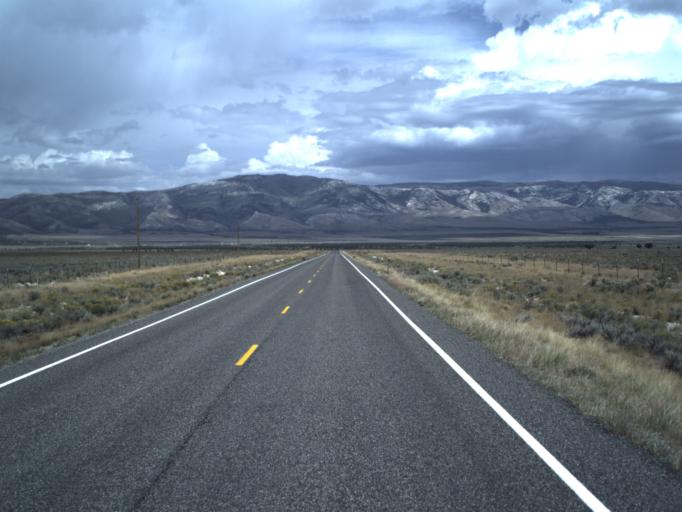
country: US
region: Idaho
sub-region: Cassia County
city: Burley
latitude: 41.7530
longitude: -113.5150
